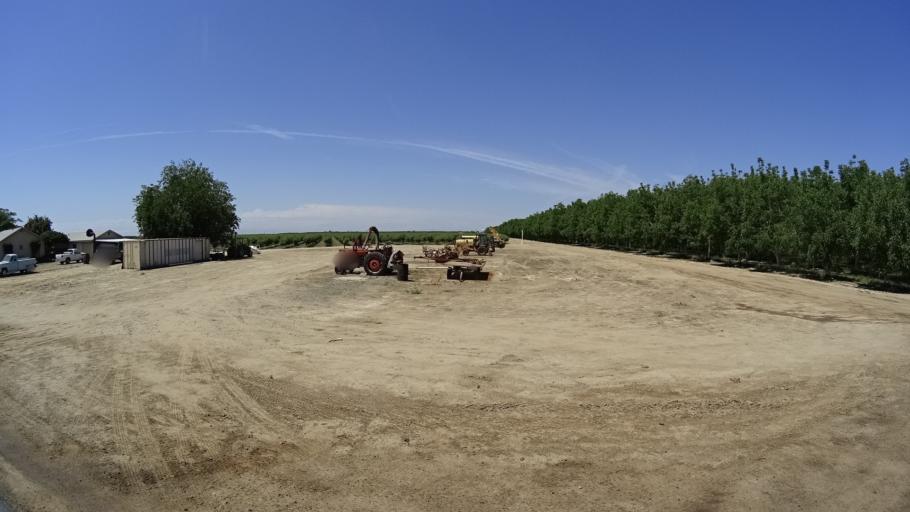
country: US
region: California
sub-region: Kings County
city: Armona
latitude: 36.2475
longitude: -119.6910
